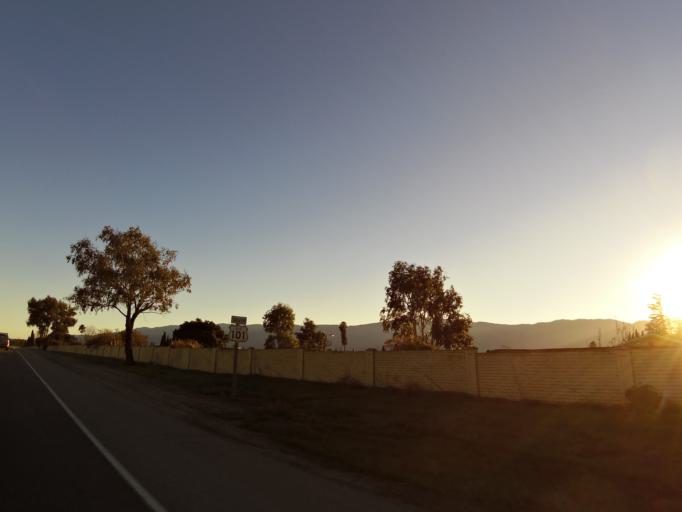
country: US
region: California
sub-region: Monterey County
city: Gonzales
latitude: 36.5102
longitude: -121.4362
